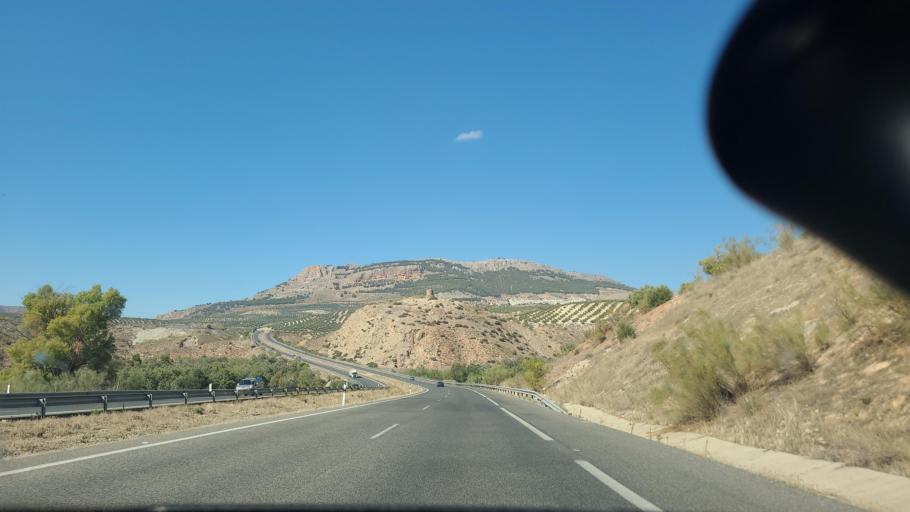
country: ES
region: Andalusia
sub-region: Provincia de Jaen
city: Pegalajar
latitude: 37.7074
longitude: -3.6383
